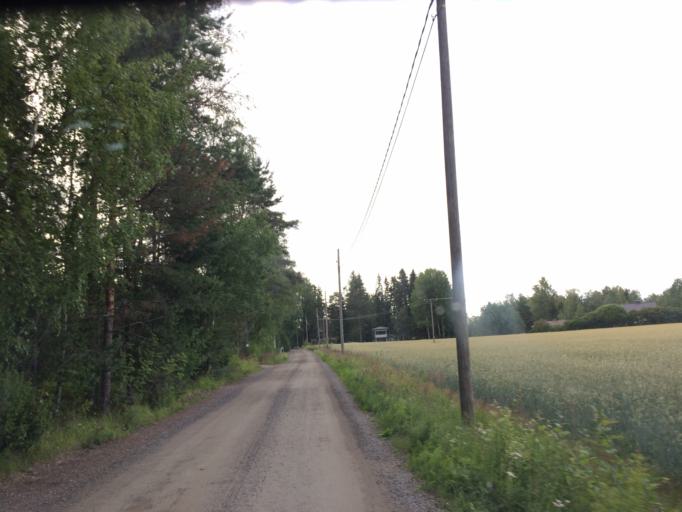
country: FI
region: Haeme
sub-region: Haemeenlinna
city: Tervakoski
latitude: 60.8528
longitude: 24.6241
